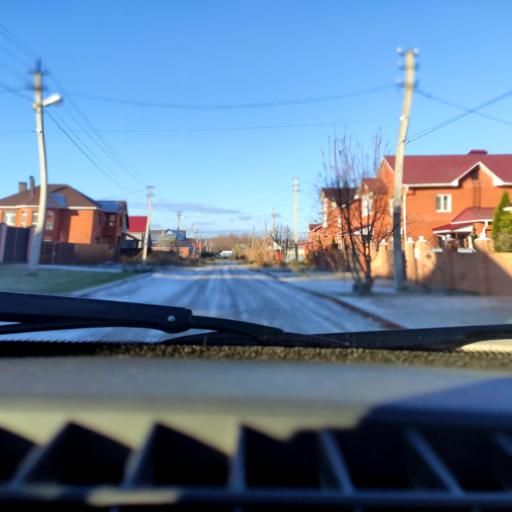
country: RU
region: Bashkortostan
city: Avdon
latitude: 54.6964
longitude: 55.7921
